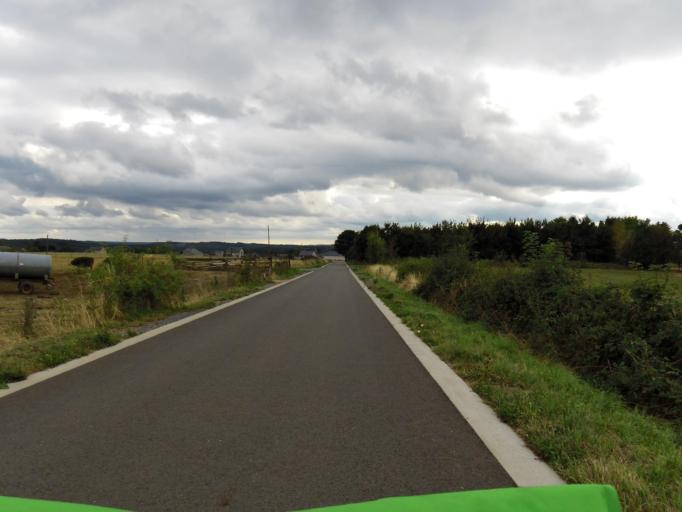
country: BE
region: Wallonia
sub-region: Province de Namur
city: Bievre
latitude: 49.9123
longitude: 4.9929
